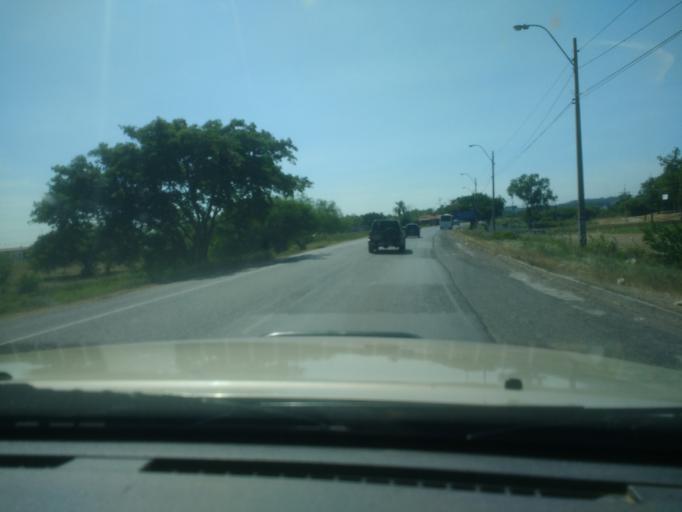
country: PY
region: Central
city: Colonia Mariano Roque Alonso
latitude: -25.1721
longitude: -57.5624
